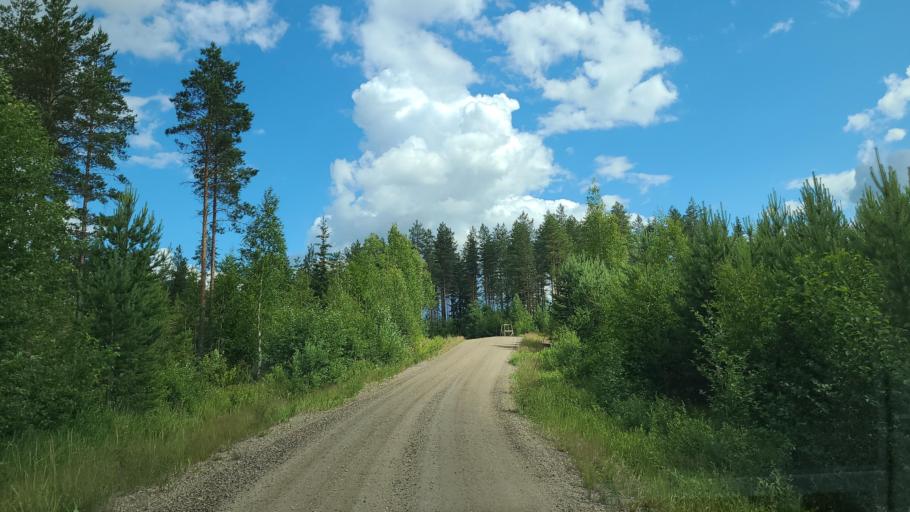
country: FI
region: Northern Savo
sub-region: Koillis-Savo
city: Kaavi
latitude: 63.0295
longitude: 28.7847
